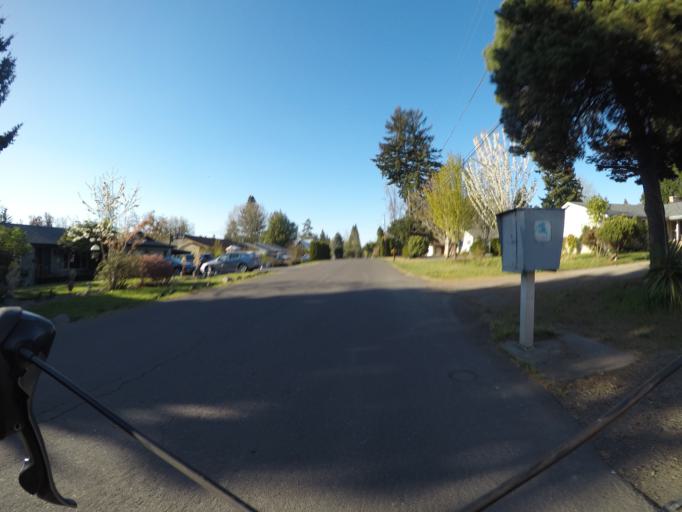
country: US
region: Oregon
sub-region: Washington County
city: Aloha
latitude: 45.4795
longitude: -122.8750
